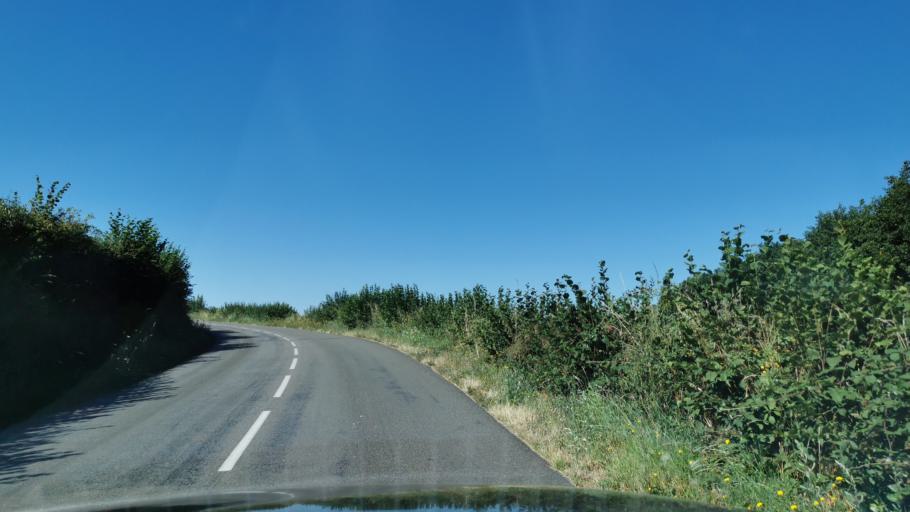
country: FR
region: Bourgogne
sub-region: Departement de Saone-et-Loire
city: Le Breuil
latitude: 46.7920
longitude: 4.4824
